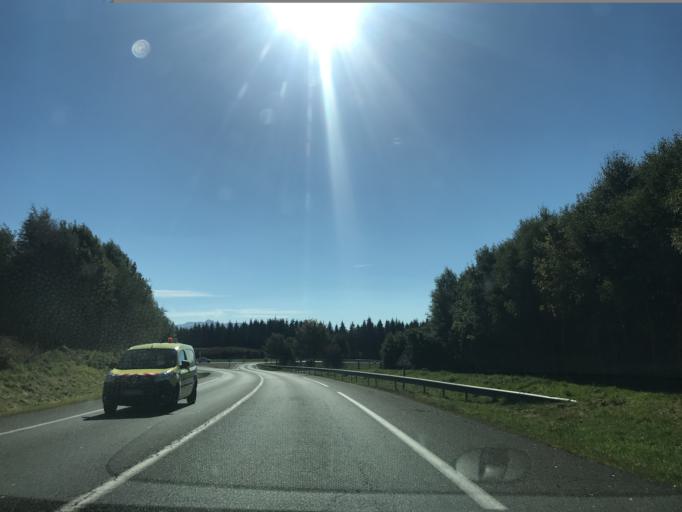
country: FR
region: Auvergne
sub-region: Departement du Puy-de-Dome
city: Saint-Sauves-d'Auvergne
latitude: 45.6573
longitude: 2.6882
